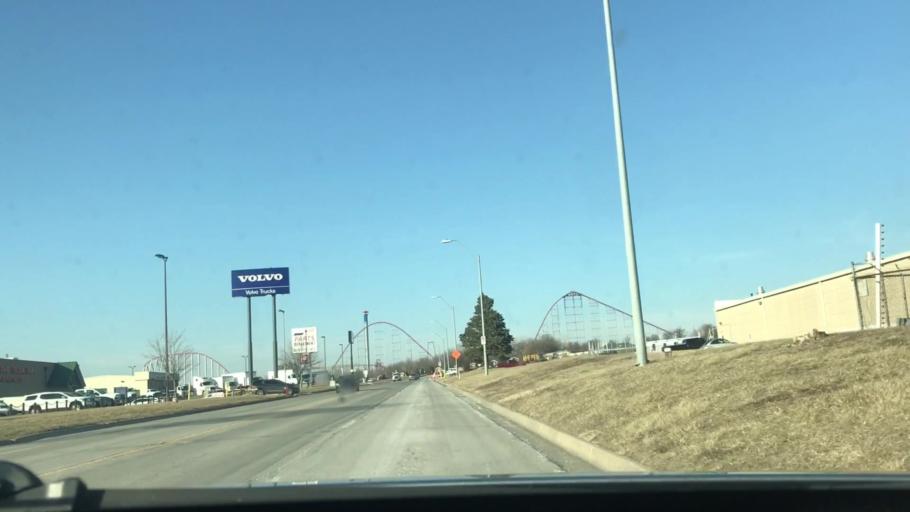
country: US
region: Missouri
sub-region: Clay County
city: Claycomo
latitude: 39.1654
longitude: -94.4886
